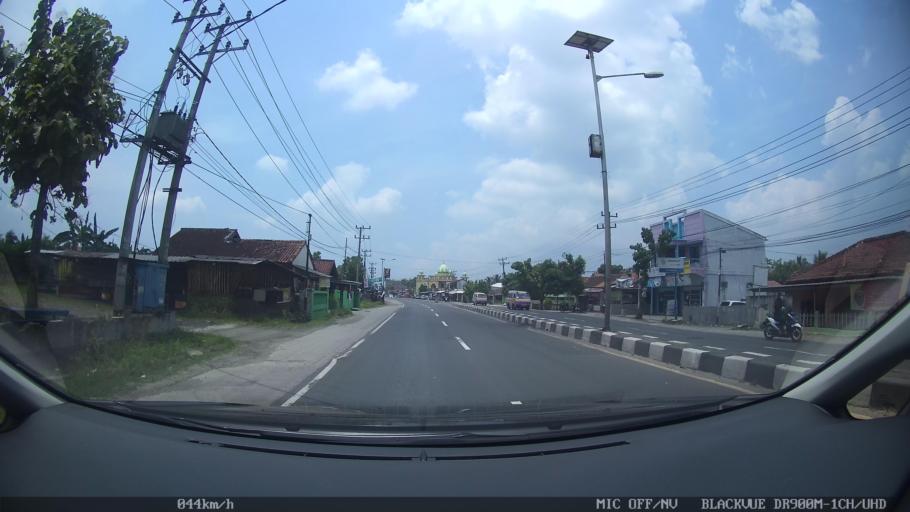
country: ID
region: Lampung
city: Natar
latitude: -5.2884
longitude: 105.1910
